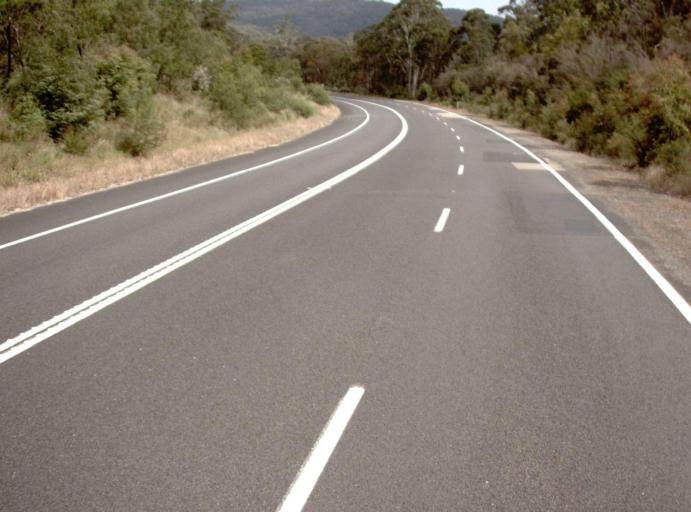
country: AU
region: New South Wales
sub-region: Bega Valley
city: Eden
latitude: -37.4628
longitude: 149.5880
